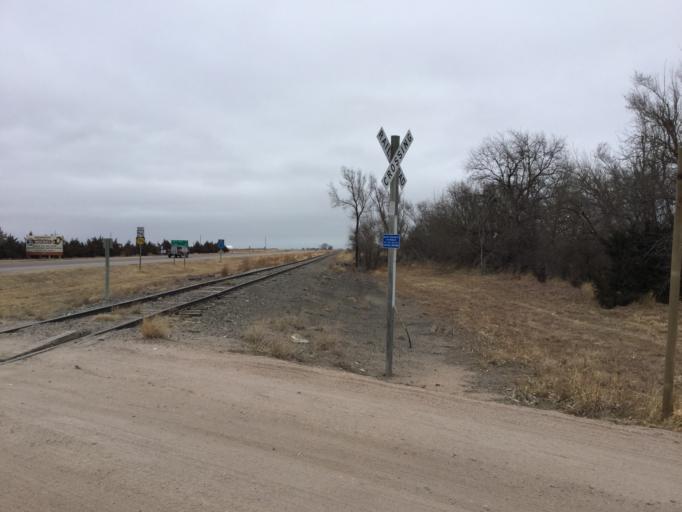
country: US
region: Kansas
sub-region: Pawnee County
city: Larned
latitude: 38.2658
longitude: -98.9770
